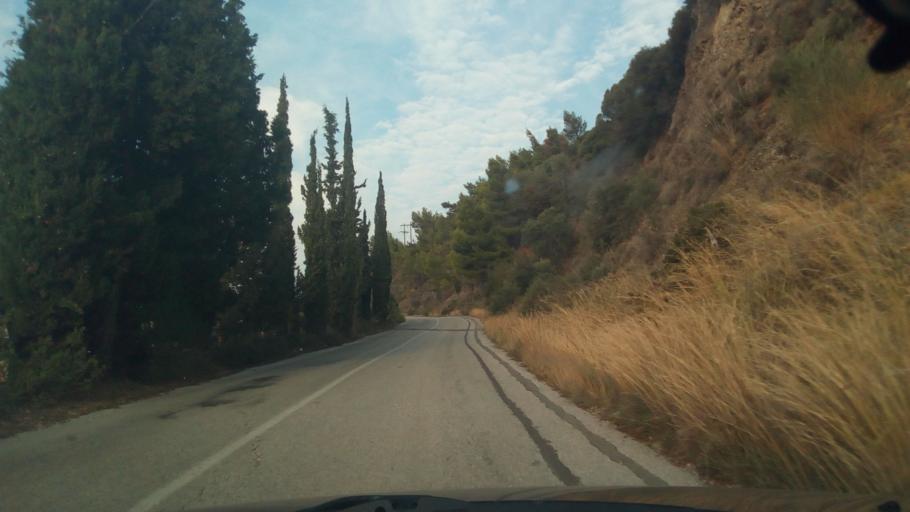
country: GR
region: West Greece
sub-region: Nomos Aitolias kai Akarnanias
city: Nafpaktos
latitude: 38.4083
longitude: 21.9412
